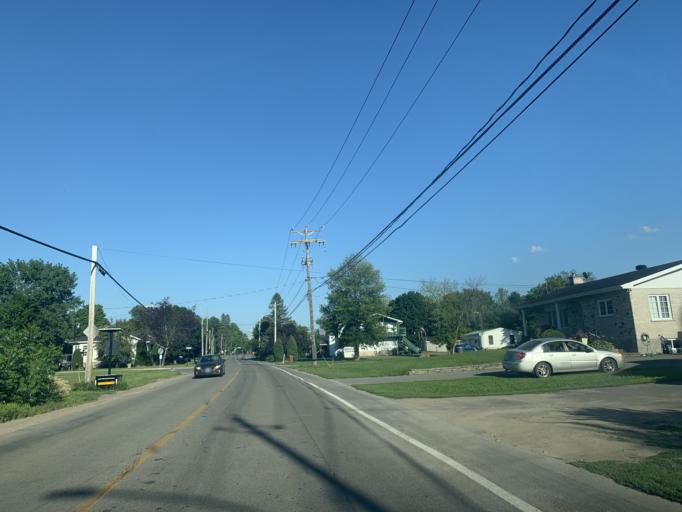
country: CA
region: Ontario
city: Hawkesbury
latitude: 45.6269
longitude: -74.5960
